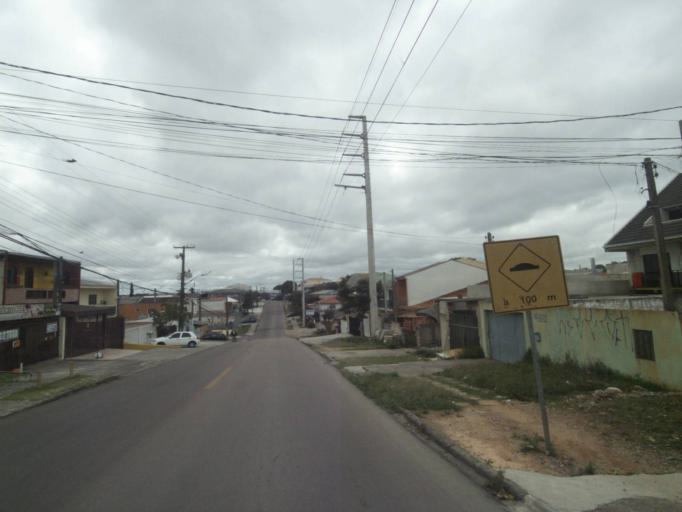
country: BR
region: Parana
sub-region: Sao Jose Dos Pinhais
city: Sao Jose dos Pinhais
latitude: -25.5468
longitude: -49.2704
